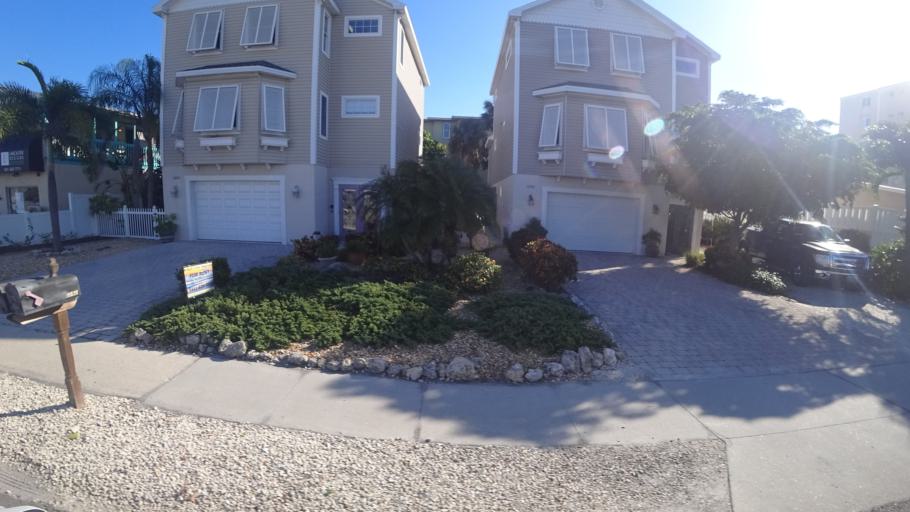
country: US
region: Florida
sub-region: Manatee County
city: Holmes Beach
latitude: 27.5058
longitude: -82.7165
